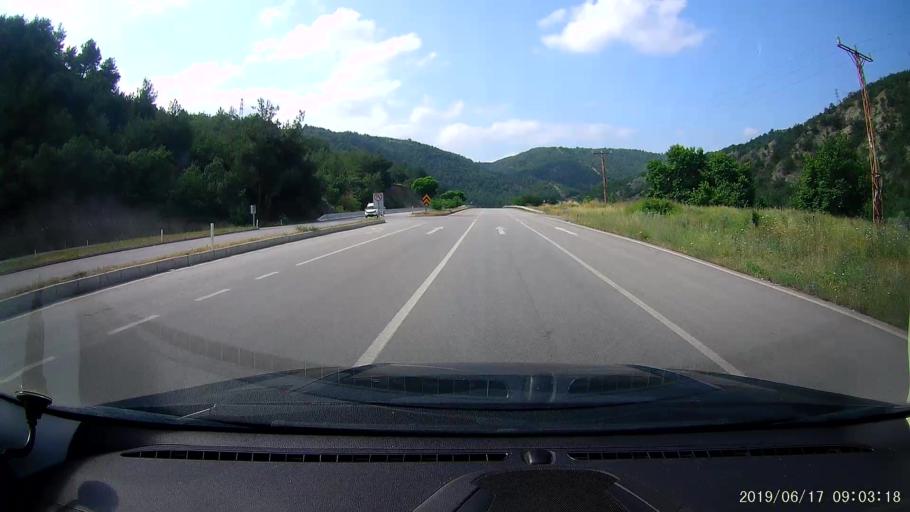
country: TR
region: Amasya
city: Tasova
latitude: 40.7575
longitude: 36.3023
